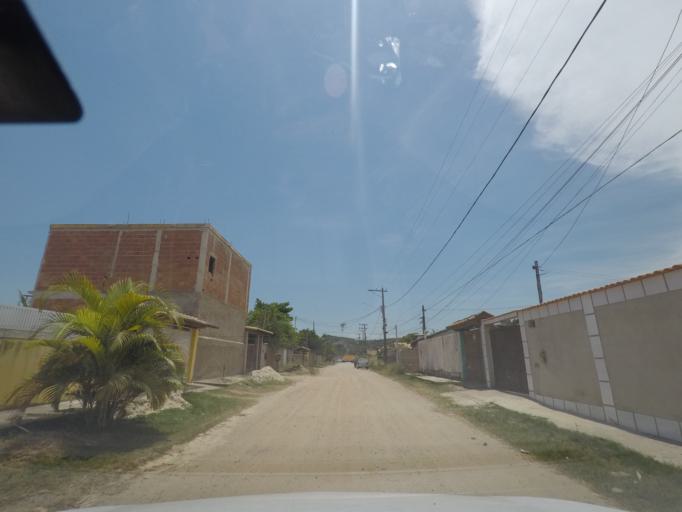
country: BR
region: Rio de Janeiro
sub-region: Marica
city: Marica
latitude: -22.9544
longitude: -42.9587
